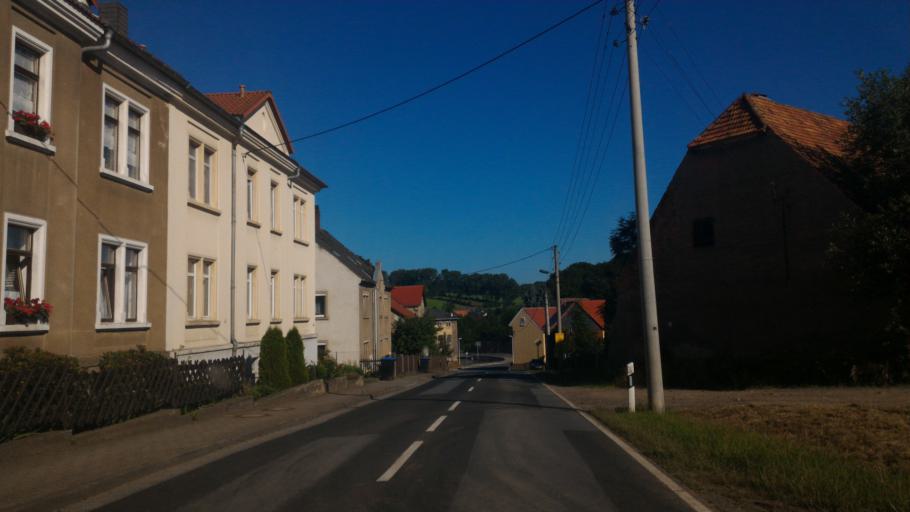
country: DE
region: Saxony
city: Mittelherwigsdorf
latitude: 50.9140
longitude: 14.7525
